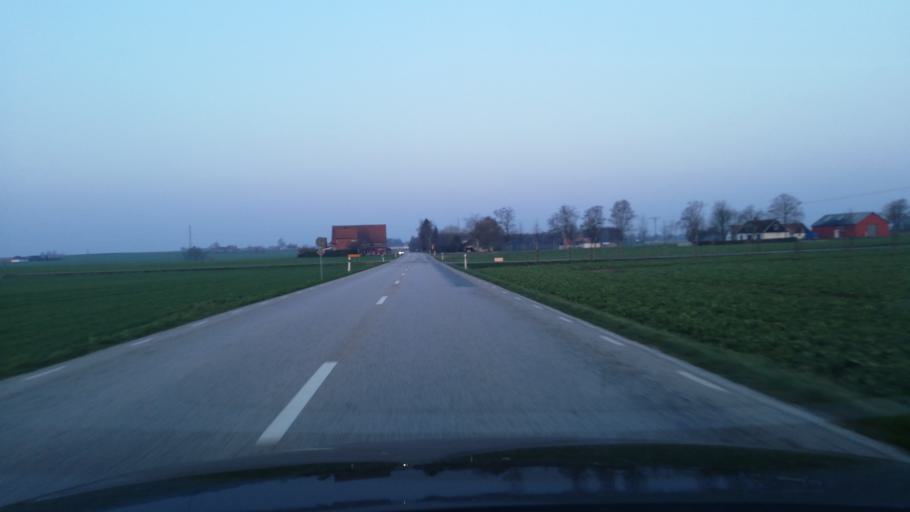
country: SE
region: Skane
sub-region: Tomelilla Kommun
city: Tomelilla
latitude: 55.4965
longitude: 14.1272
